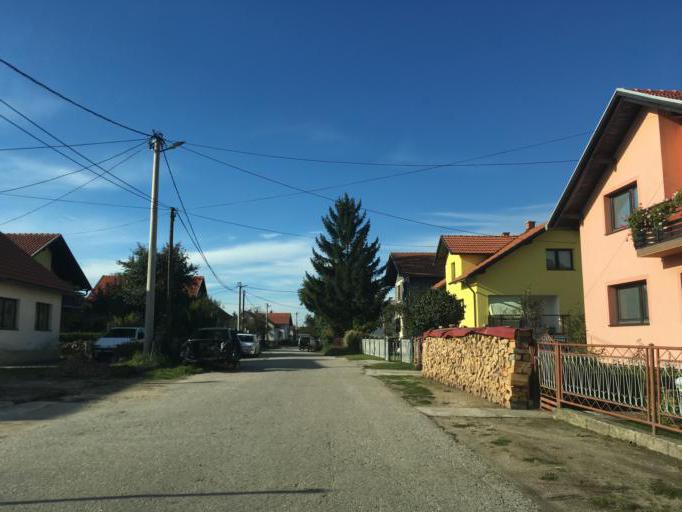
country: BA
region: Federation of Bosnia and Herzegovina
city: Bugojno
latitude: 44.0604
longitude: 17.4595
